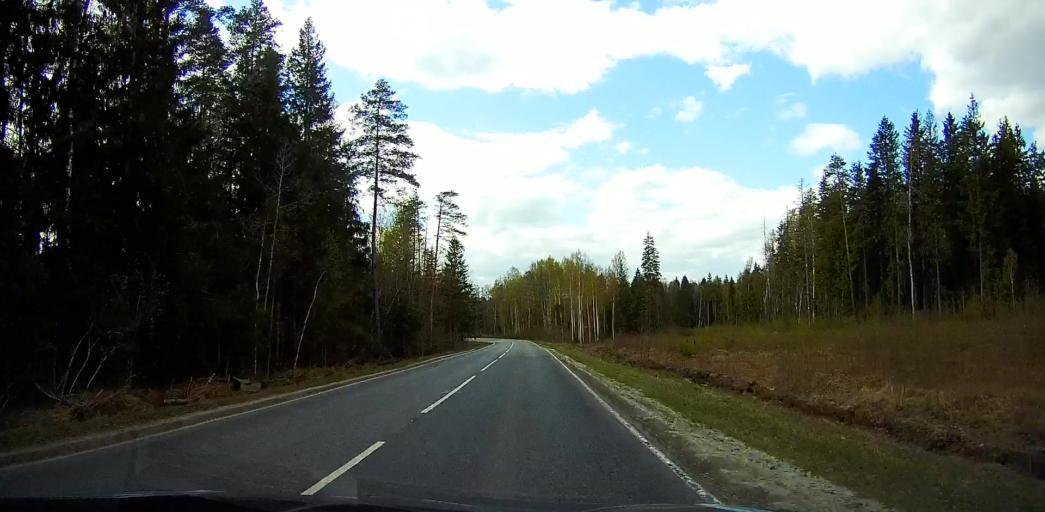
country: RU
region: Moskovskaya
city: Rakhmanovo
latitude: 55.6511
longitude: 38.6591
